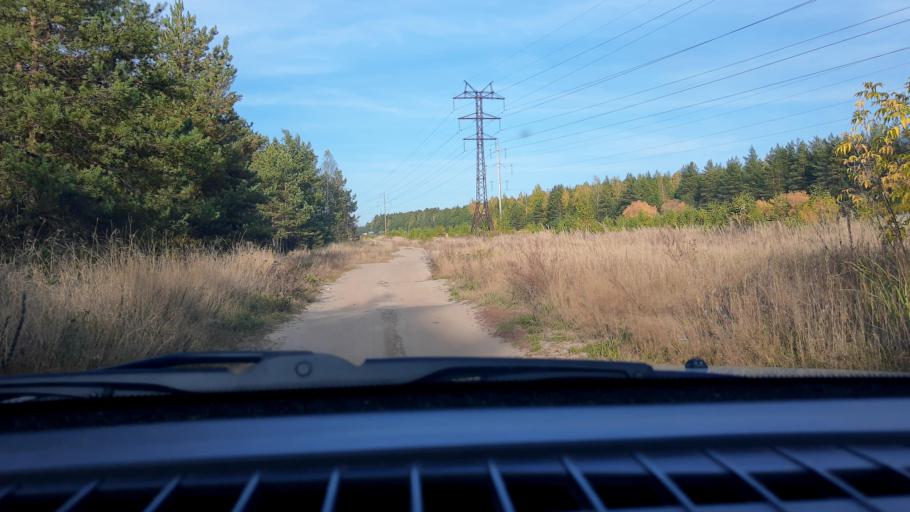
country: RU
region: Nizjnij Novgorod
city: Lukino
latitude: 56.3948
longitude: 43.6447
